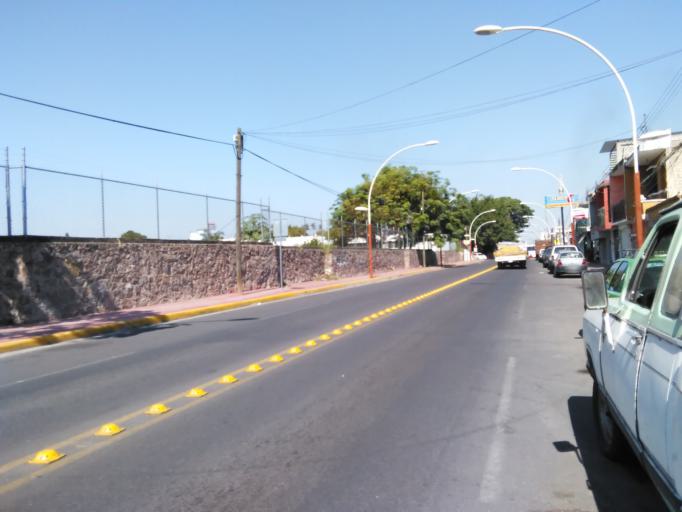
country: MX
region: Nayarit
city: Tepic
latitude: 21.4938
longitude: -104.8896
